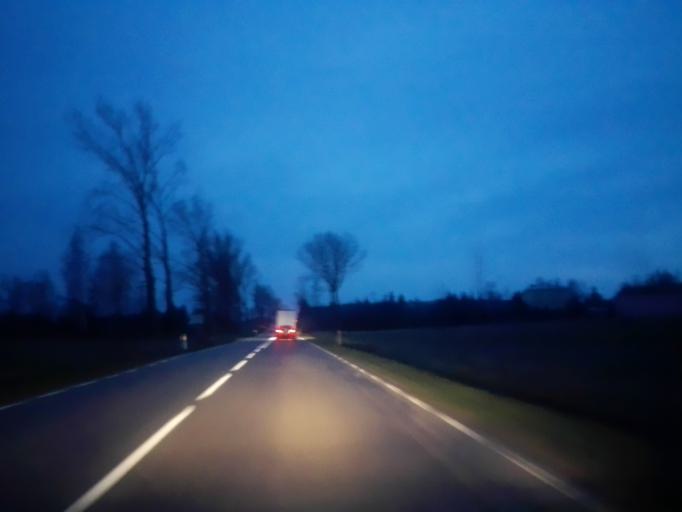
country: PL
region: Podlasie
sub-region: Lomza
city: Lomza
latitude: 53.1116
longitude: 22.0296
